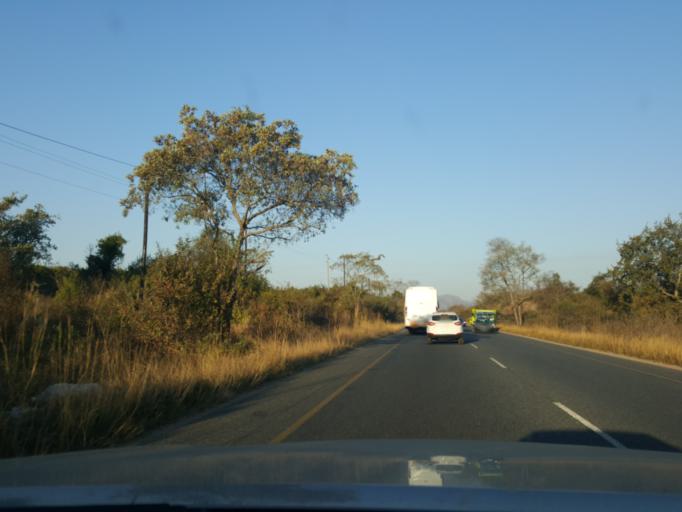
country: ZA
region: Mpumalanga
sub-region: Ehlanzeni District
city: Nelspruit
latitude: -25.4629
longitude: 31.0758
